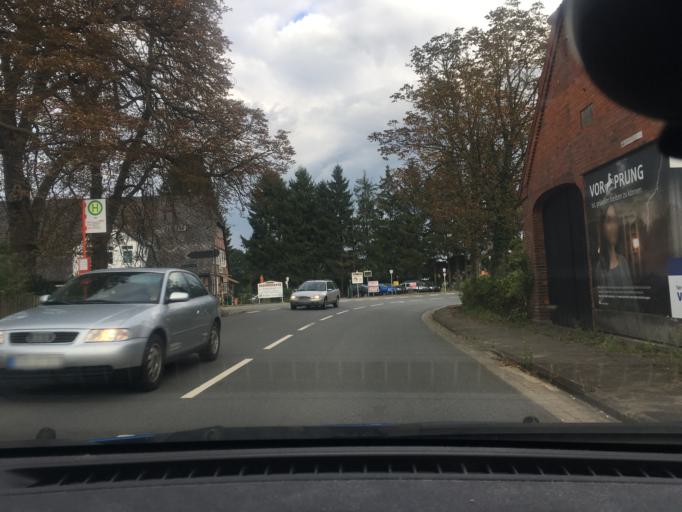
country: DE
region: Lower Saxony
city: Nahrendorf
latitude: 53.1588
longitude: 10.8103
